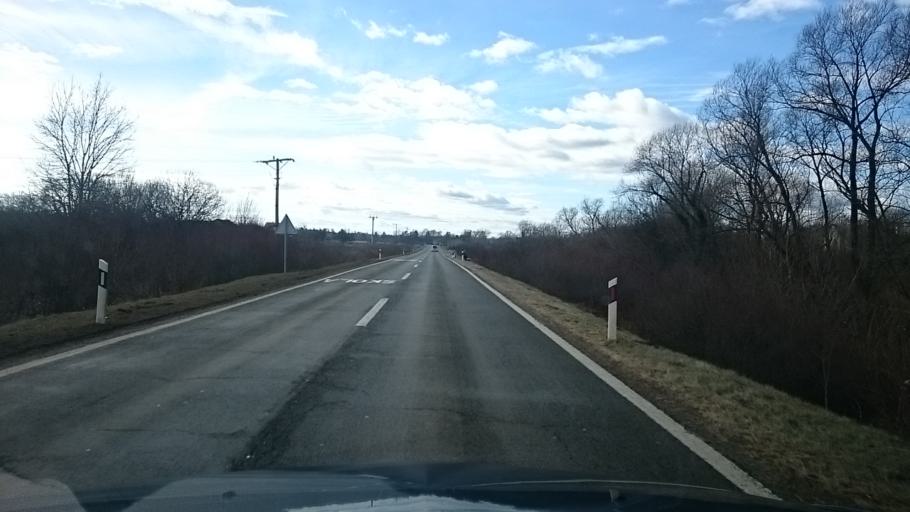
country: HR
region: Sisacko-Moslavacka
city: Novska
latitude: 45.2780
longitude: 16.9170
